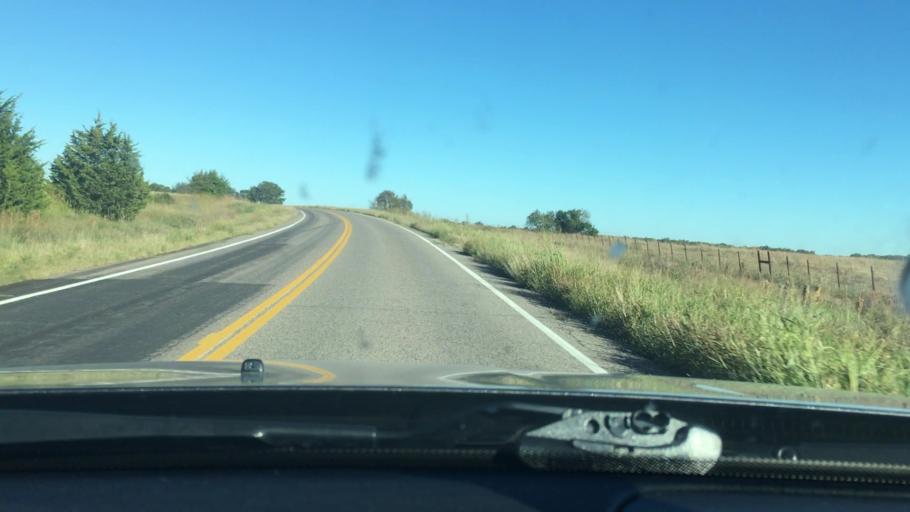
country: US
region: Oklahoma
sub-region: Johnston County
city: Tishomingo
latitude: 34.1617
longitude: -96.7060
